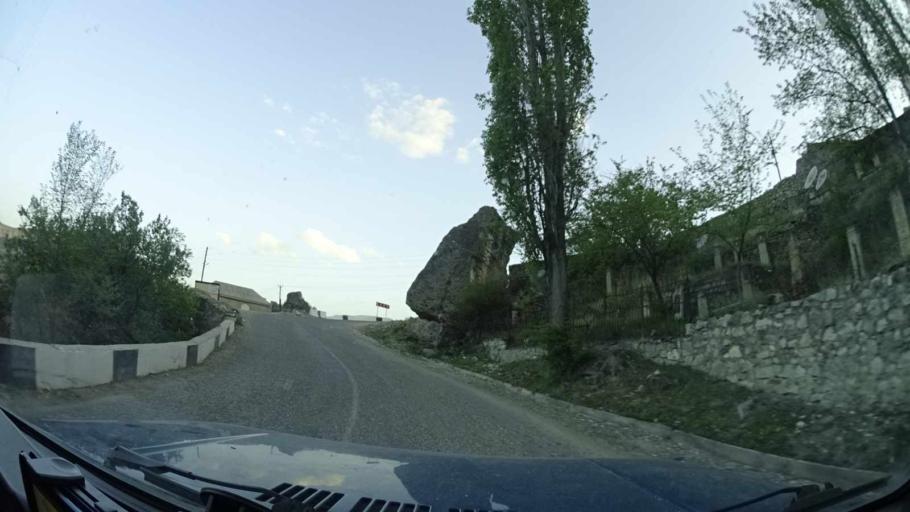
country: RU
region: Dagestan
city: Gunib
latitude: 42.3858
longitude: 46.9597
